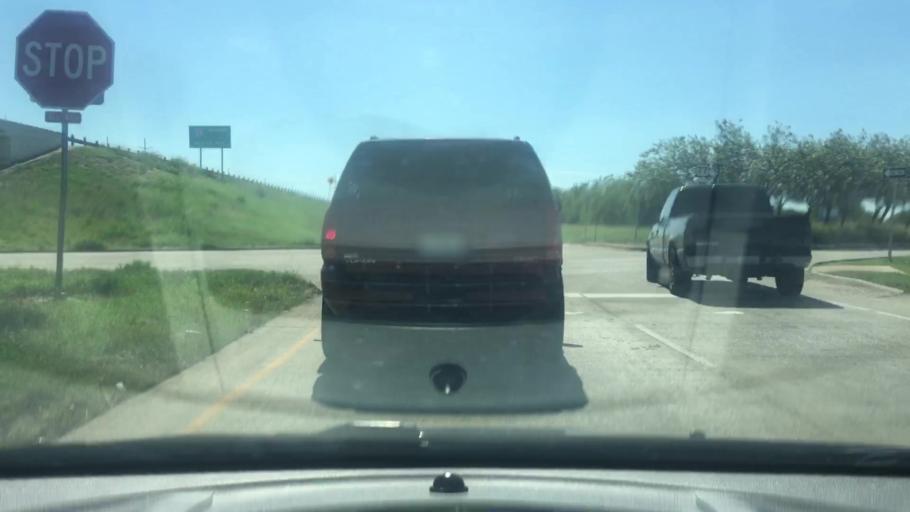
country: US
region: Texas
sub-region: Denton County
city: Denton
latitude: 33.2582
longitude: -97.1651
